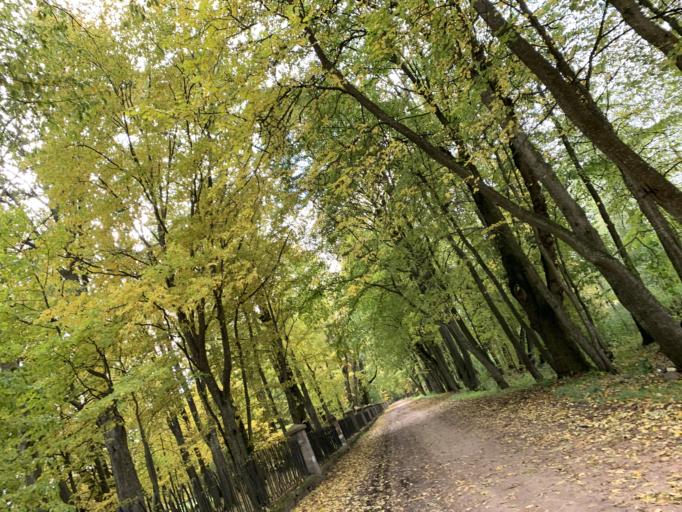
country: BY
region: Minsk
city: Nyasvizh
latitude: 53.2306
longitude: 26.6983
